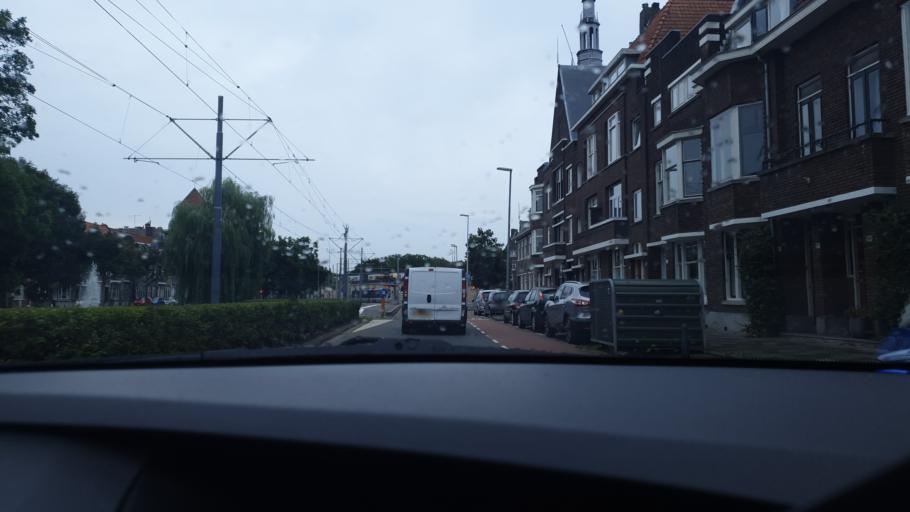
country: NL
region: South Holland
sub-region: Gemeente Barendrecht
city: Barendrecht
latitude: 51.8915
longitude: 4.5127
